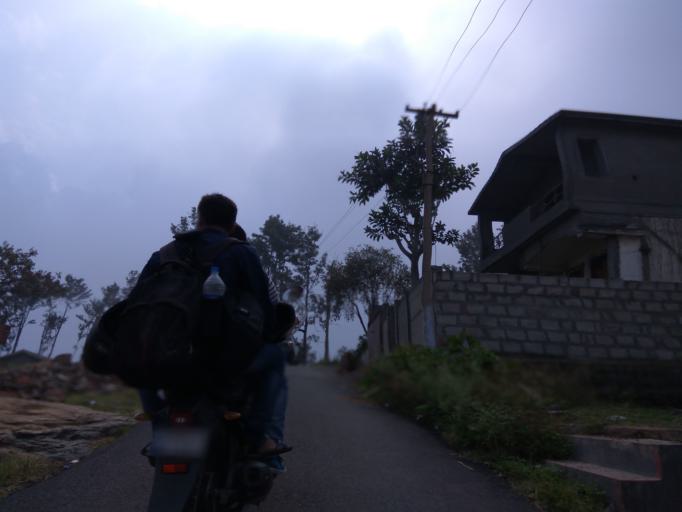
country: IN
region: Tamil Nadu
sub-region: Salem
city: Salem
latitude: 11.7681
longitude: 78.2395
